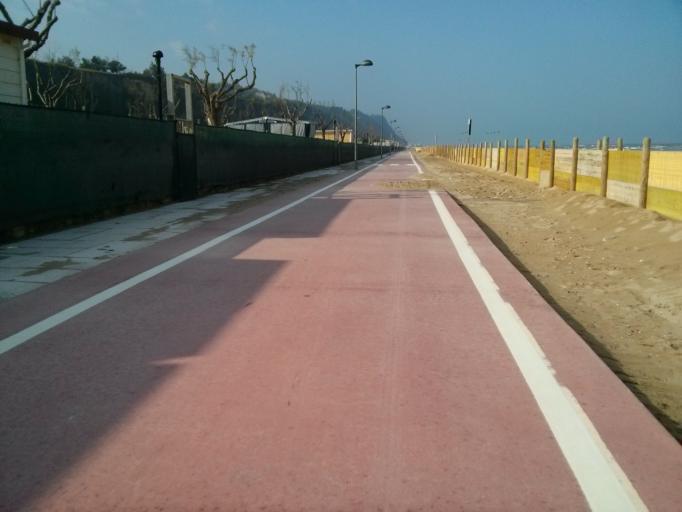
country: IT
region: The Marches
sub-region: Provincia di Pesaro e Urbino
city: Fenile
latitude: 43.8823
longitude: 12.9612
